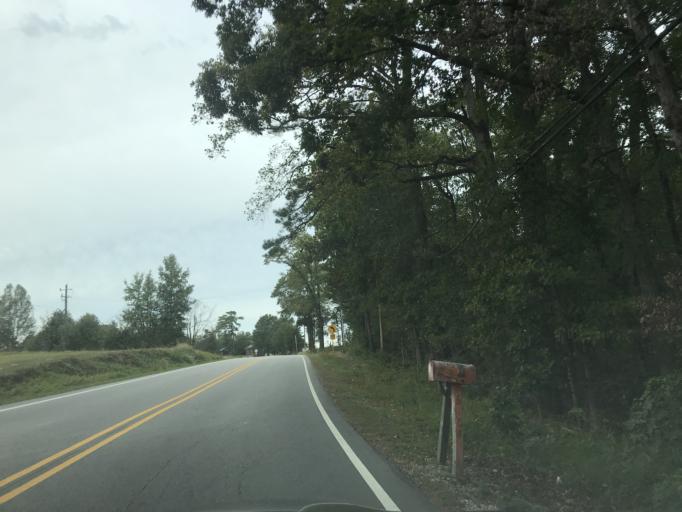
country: US
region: North Carolina
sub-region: Wake County
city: Knightdale
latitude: 35.8231
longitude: -78.5047
